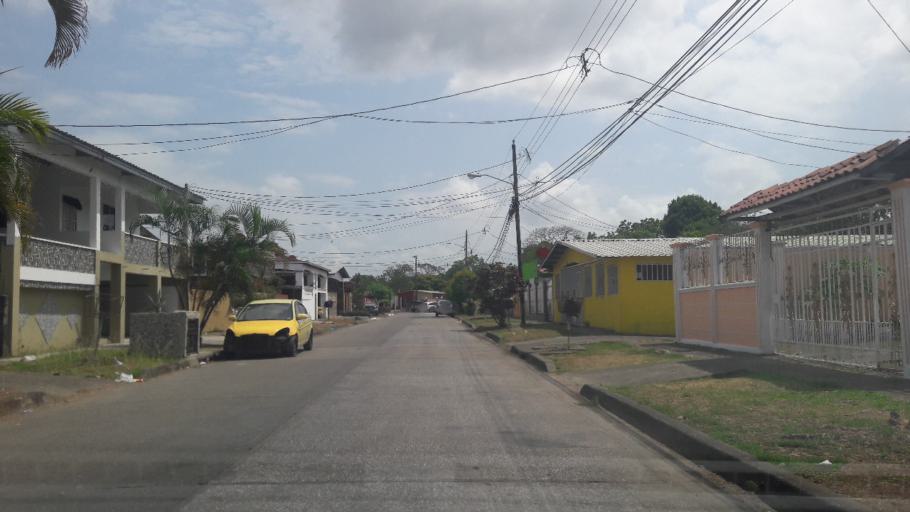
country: PA
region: Panama
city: Alcalde Diaz
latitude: 9.1376
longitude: -79.5515
